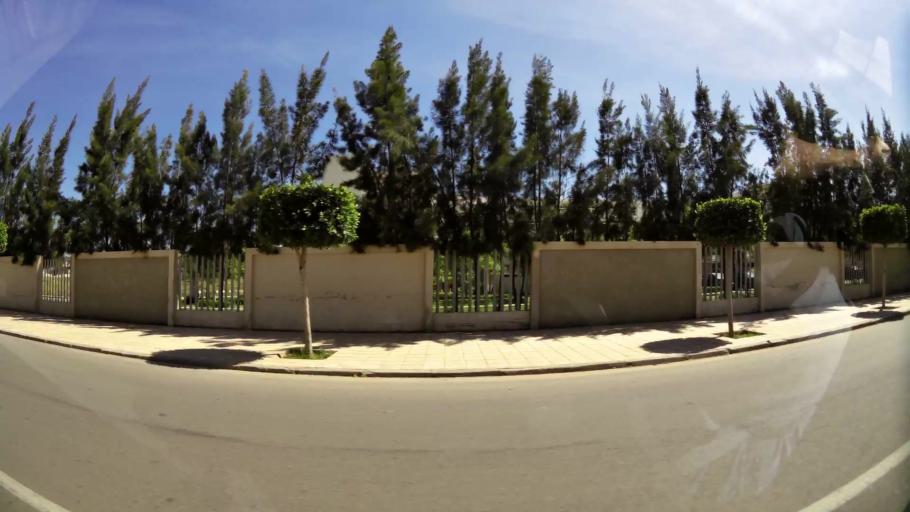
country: MA
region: Oriental
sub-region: Oujda-Angad
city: Oujda
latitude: 34.6573
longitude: -1.9104
